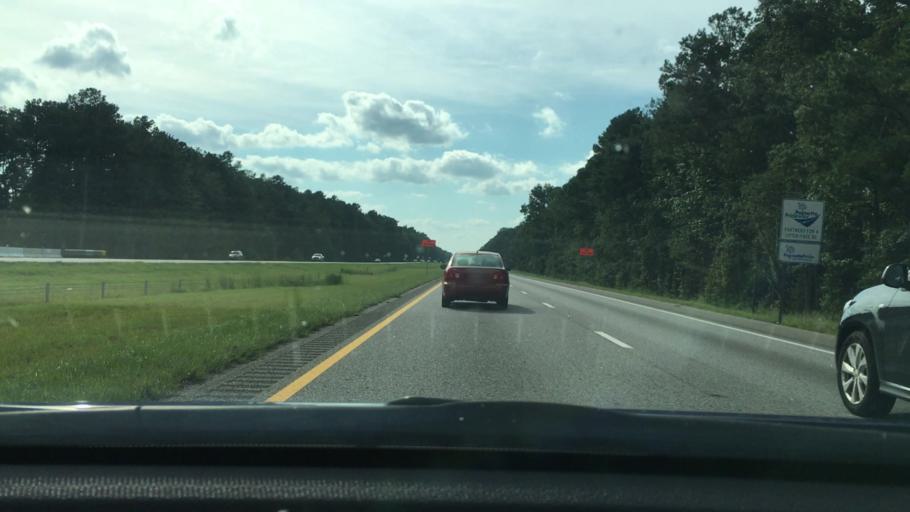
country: US
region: South Carolina
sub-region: Dorchester County
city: Ridgeville
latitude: 33.1259
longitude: -80.2867
